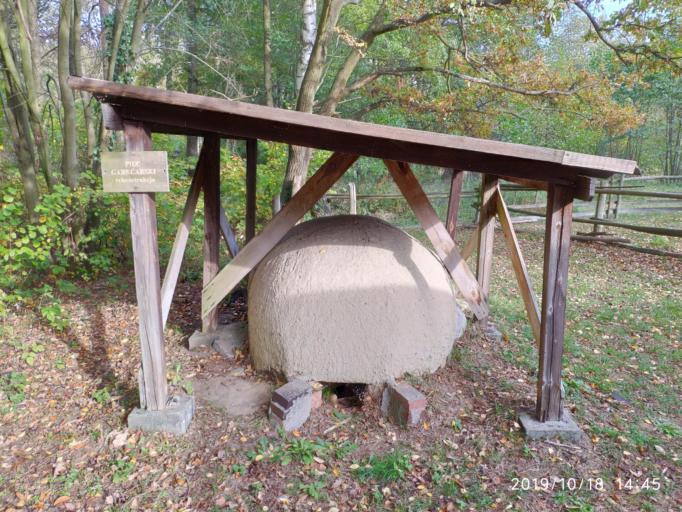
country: PL
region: Lubusz
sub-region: Powiat zielonogorski
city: Ochla
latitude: 51.8910
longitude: 15.4710
